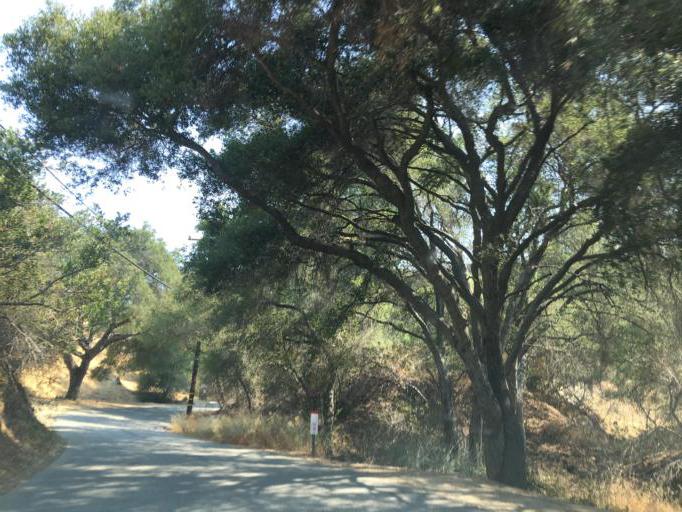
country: US
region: California
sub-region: Los Angeles County
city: Topanga
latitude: 34.1131
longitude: -118.6264
